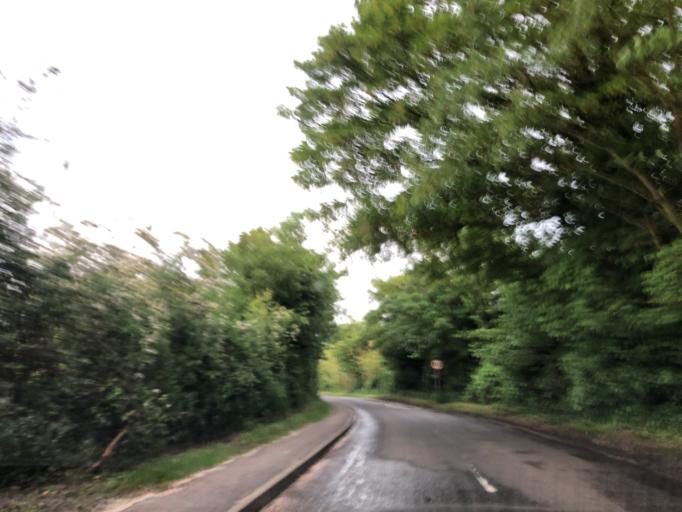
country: GB
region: England
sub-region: Warwickshire
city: Warwick
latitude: 52.2750
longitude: -1.6297
